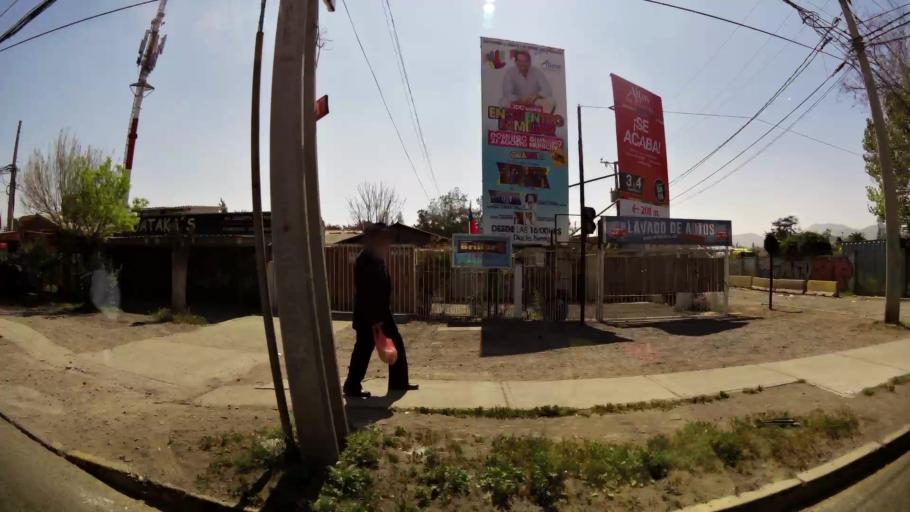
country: CL
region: Santiago Metropolitan
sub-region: Provincia de Santiago
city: Lo Prado
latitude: -33.3661
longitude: -70.7066
